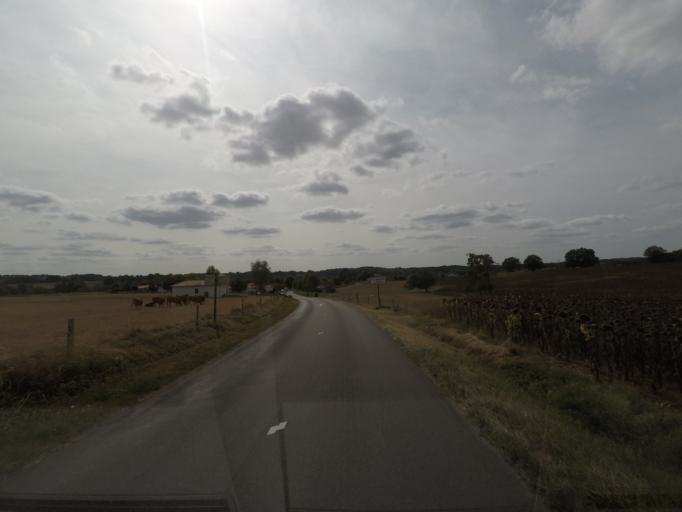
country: FR
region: Poitou-Charentes
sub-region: Departement de la Charente
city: Saint-Claud
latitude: 45.9428
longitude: 0.4880
